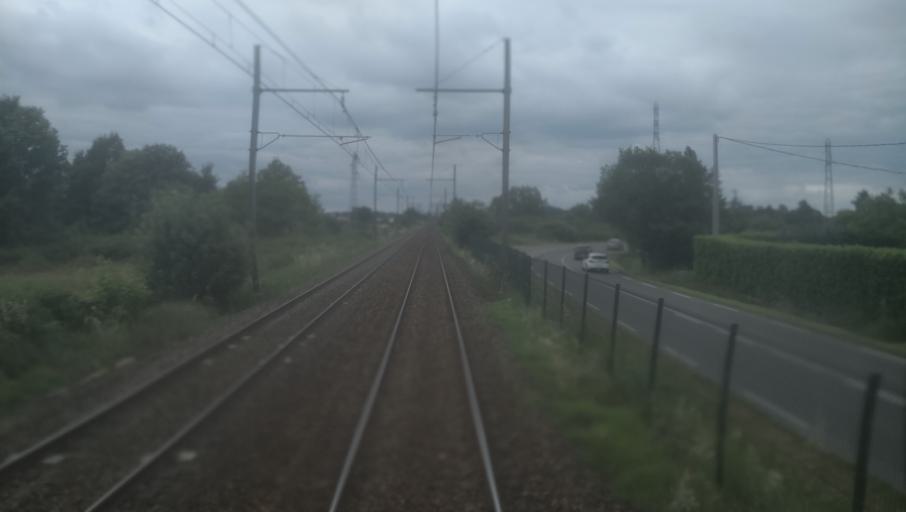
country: FR
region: Midi-Pyrenees
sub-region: Departement du Tarn-et-Garonne
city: Montbeton
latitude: 44.0153
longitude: 1.3130
